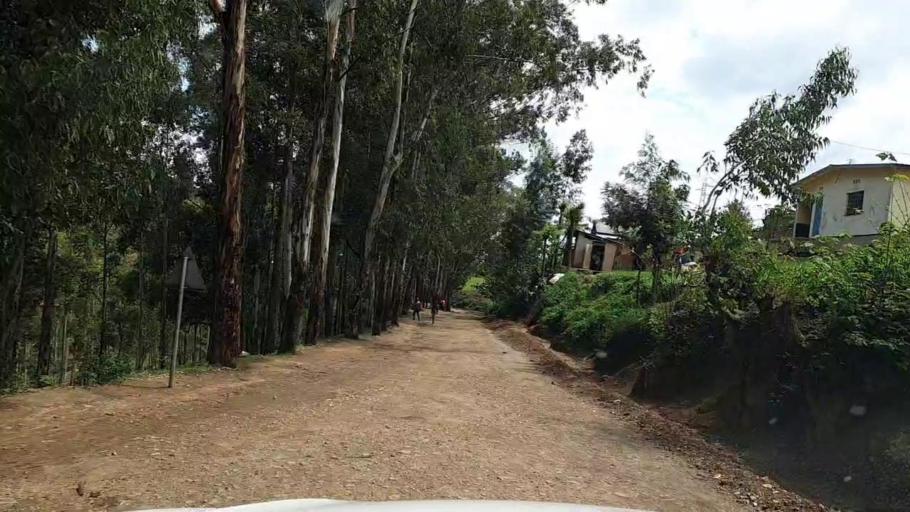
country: RW
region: Southern Province
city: Gikongoro
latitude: -2.3282
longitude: 29.5311
